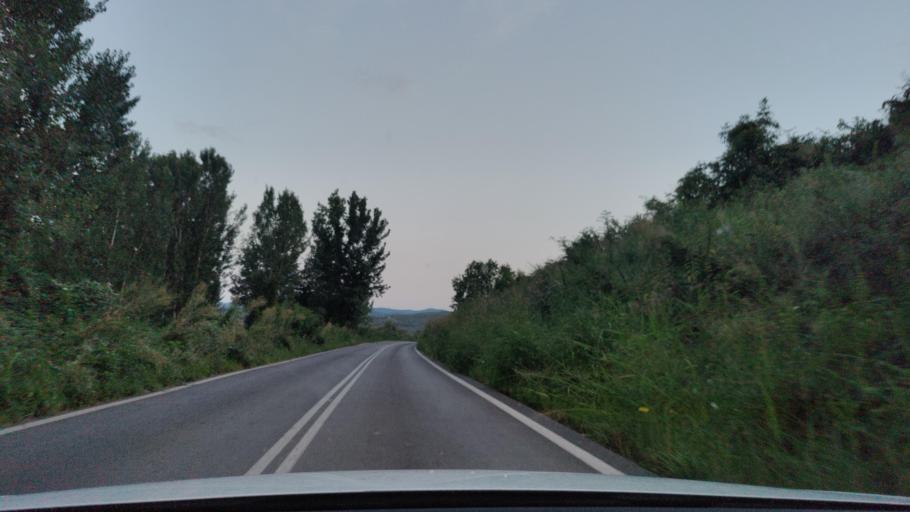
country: GR
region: Central Macedonia
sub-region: Nomos Serron
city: Chrysochorafa
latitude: 41.1419
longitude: 23.2286
